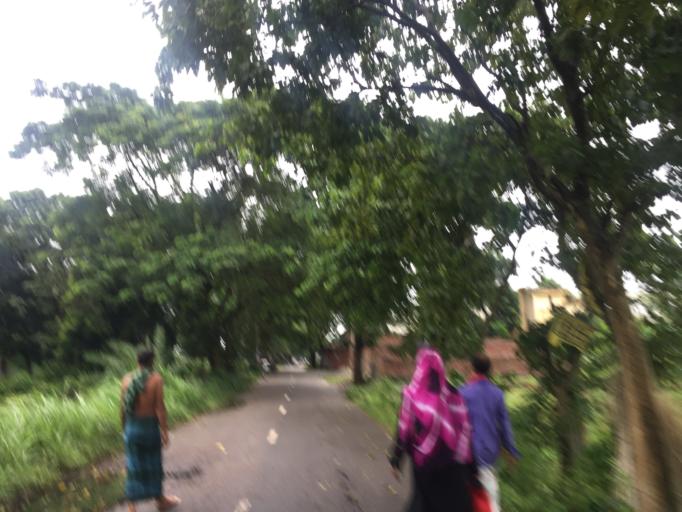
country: BD
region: Dhaka
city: Narayanganj
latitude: 23.5132
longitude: 90.4697
